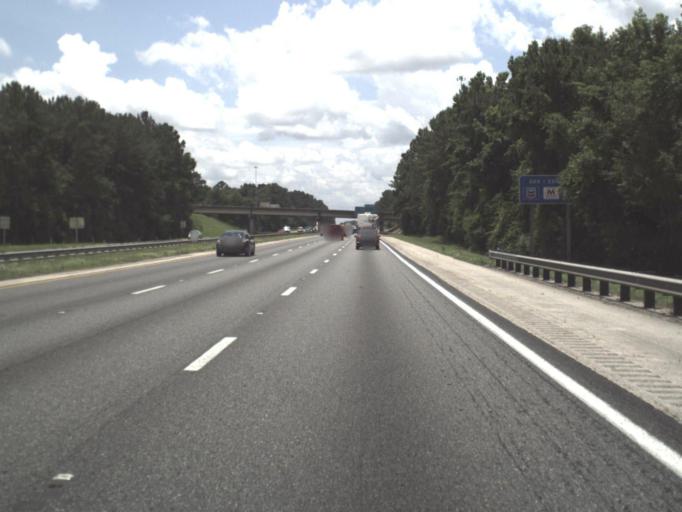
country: US
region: Florida
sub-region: Alachua County
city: High Springs
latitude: 29.8770
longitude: -82.5431
